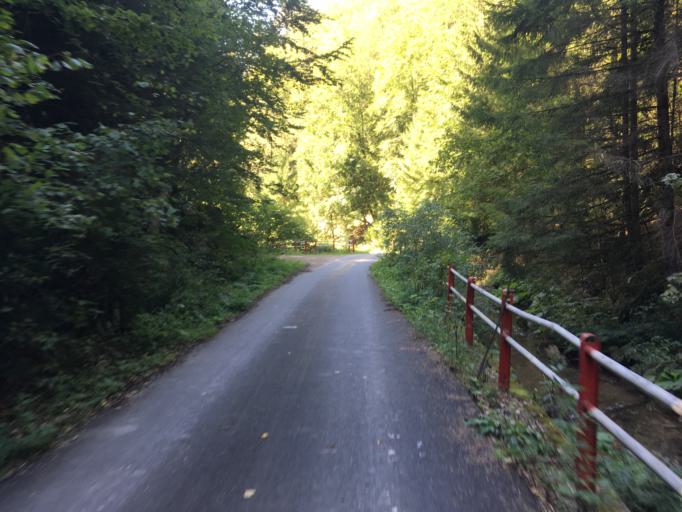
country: SK
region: Trenciansky
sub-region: Okres Povazska Bystrica
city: Povazska Bystrica
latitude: 49.0071
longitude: 18.4600
